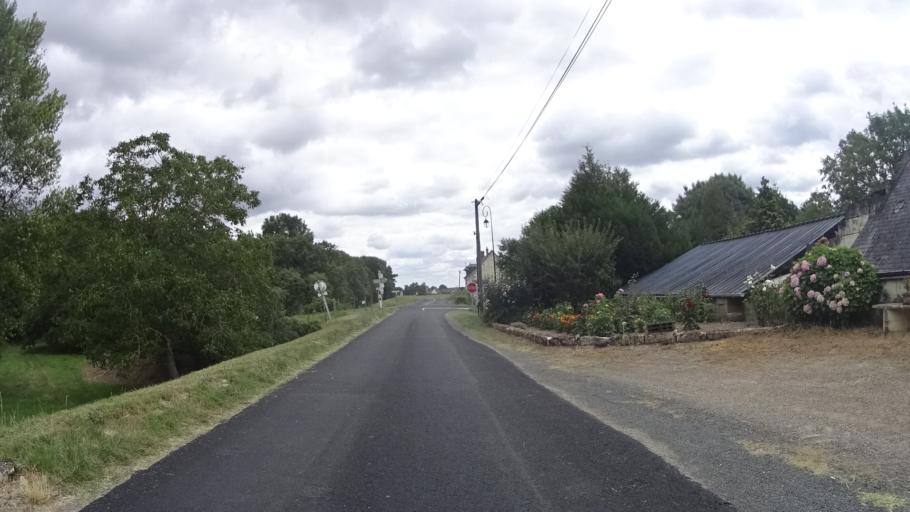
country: FR
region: Centre
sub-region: Departement d'Indre-et-Loire
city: Huismes
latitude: 47.2611
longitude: 0.2870
